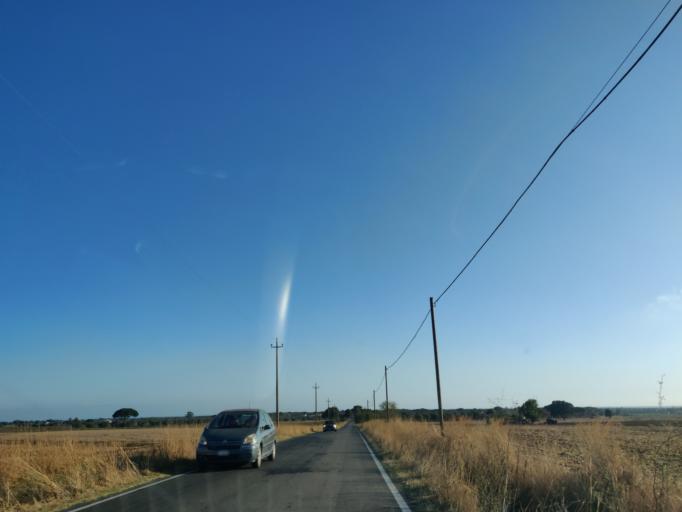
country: IT
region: Latium
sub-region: Provincia di Viterbo
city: Montalto di Castro
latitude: 42.3078
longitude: 11.6529
